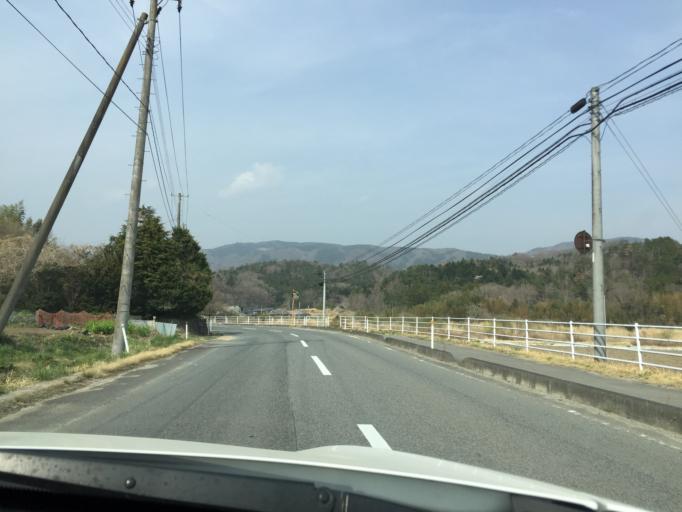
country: JP
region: Fukushima
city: Iwaki
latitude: 37.0126
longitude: 140.7364
